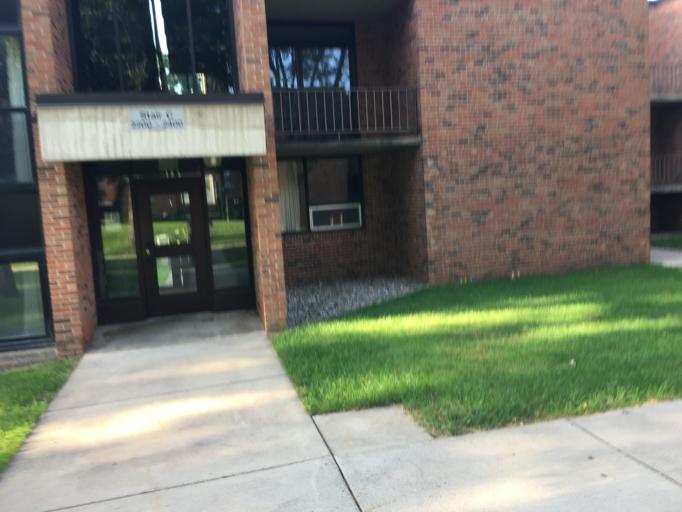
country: US
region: Minnesota
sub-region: Stearns County
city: Saint Cloud
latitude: 45.5555
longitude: -94.1501
